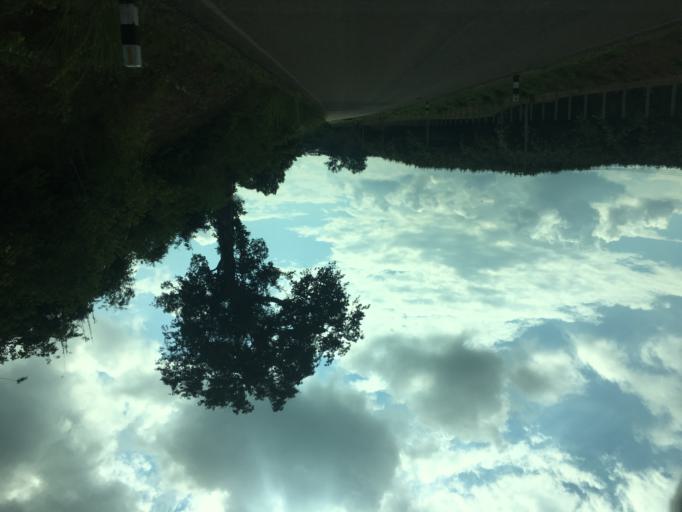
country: TH
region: Nong Khai
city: Sangkhom
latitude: 18.1912
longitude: 102.2126
